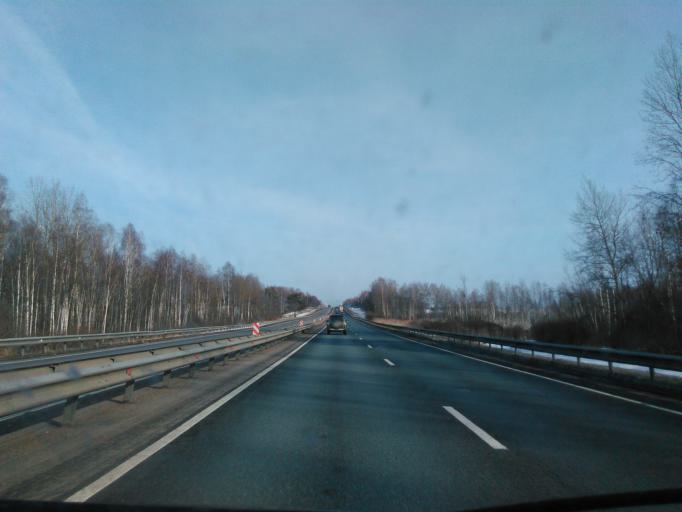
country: RU
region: Smolensk
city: Verkhnedneprovskiy
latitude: 55.1823
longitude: 33.5351
